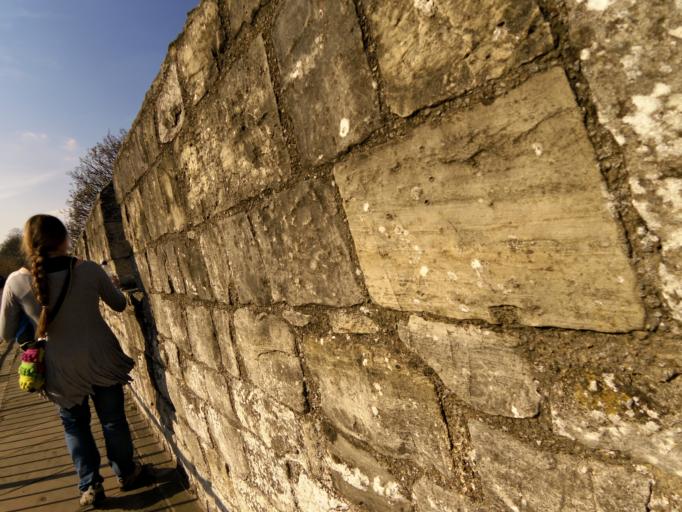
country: GB
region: England
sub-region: City of York
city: York
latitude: 53.9631
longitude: -1.0791
